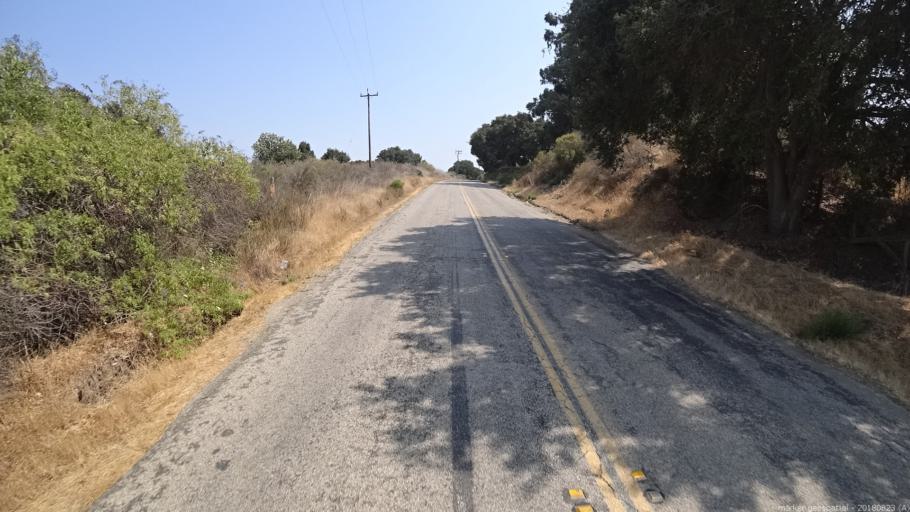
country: US
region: California
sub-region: Monterey County
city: Gonzales
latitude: 36.4476
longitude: -121.4337
